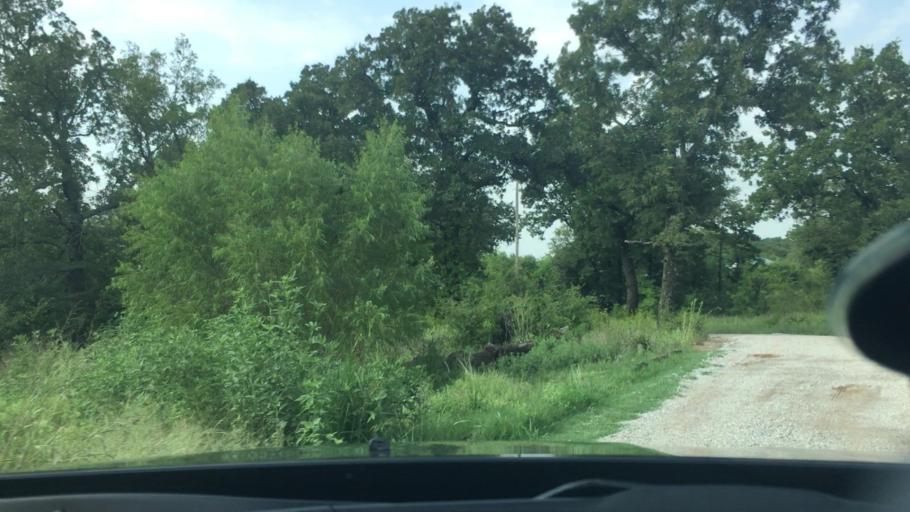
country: US
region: Oklahoma
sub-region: Carter County
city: Lone Grove
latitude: 34.2315
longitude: -97.2674
